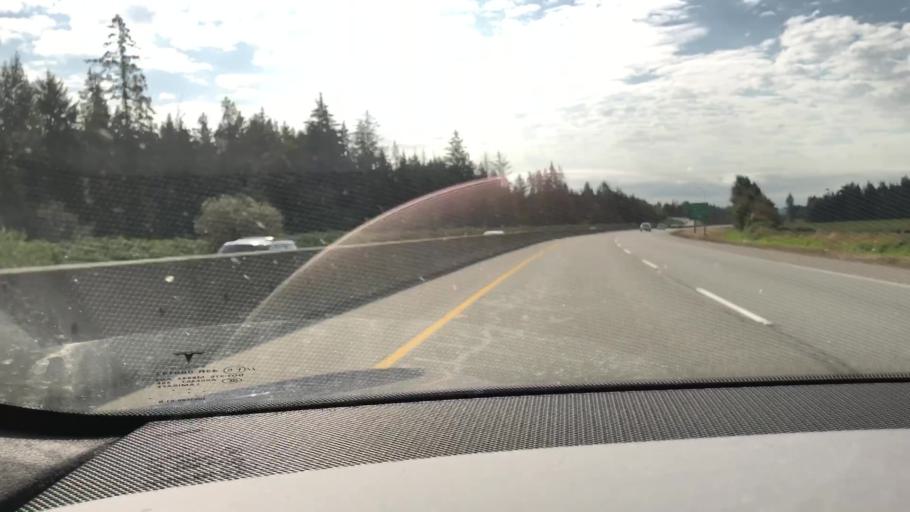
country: CA
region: British Columbia
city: Delta
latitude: 49.1102
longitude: -122.9057
